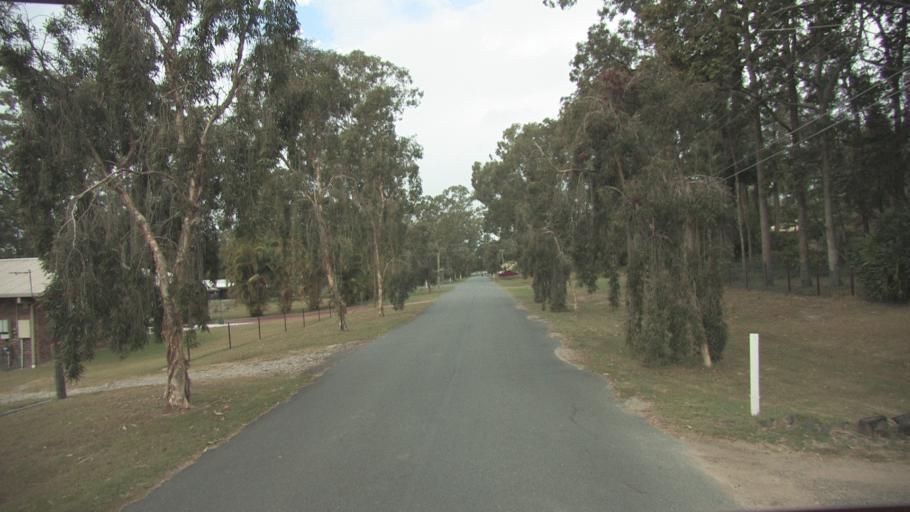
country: AU
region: Queensland
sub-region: Logan
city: Park Ridge South
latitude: -27.6828
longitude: 153.0133
